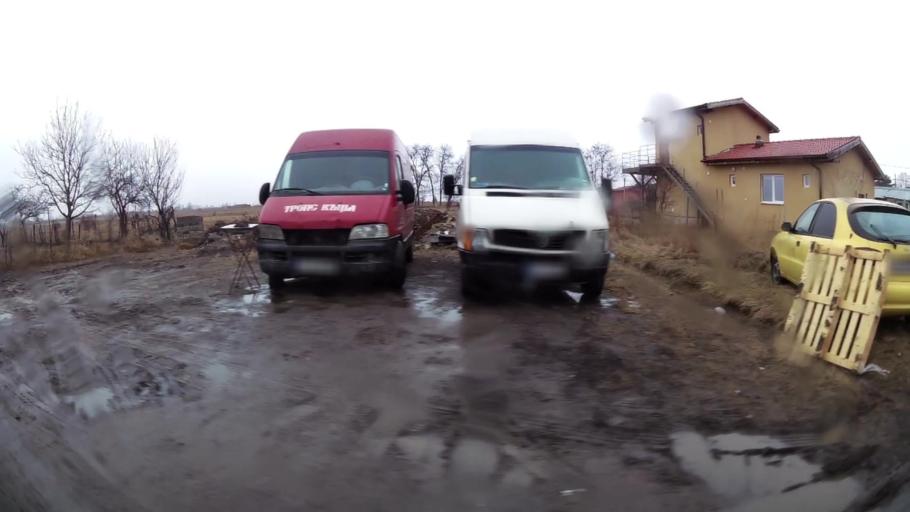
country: BG
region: Sofia-Capital
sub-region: Stolichna Obshtina
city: Sofia
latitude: 42.6584
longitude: 23.4288
